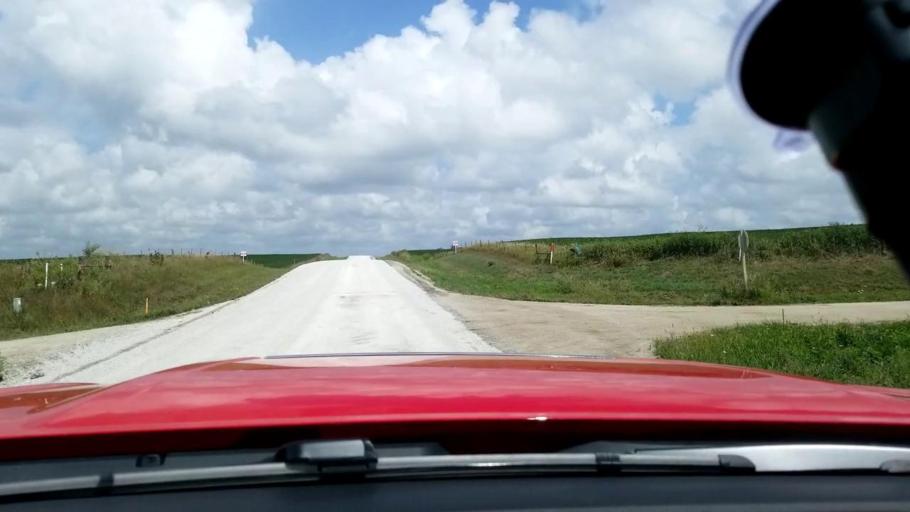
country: US
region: Iowa
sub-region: Decatur County
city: Lamoni
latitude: 40.6672
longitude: -94.0483
